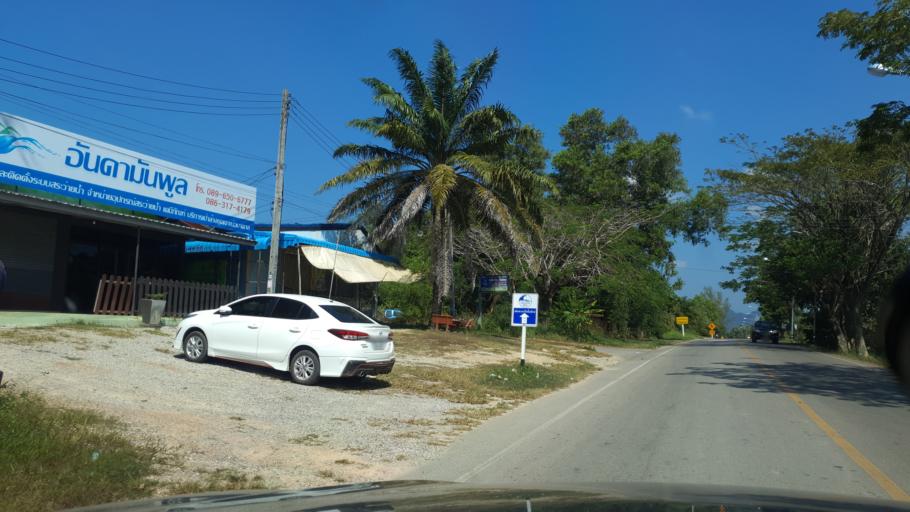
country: TH
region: Phangnga
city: Ban Ao Nang
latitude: 8.0393
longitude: 98.8616
